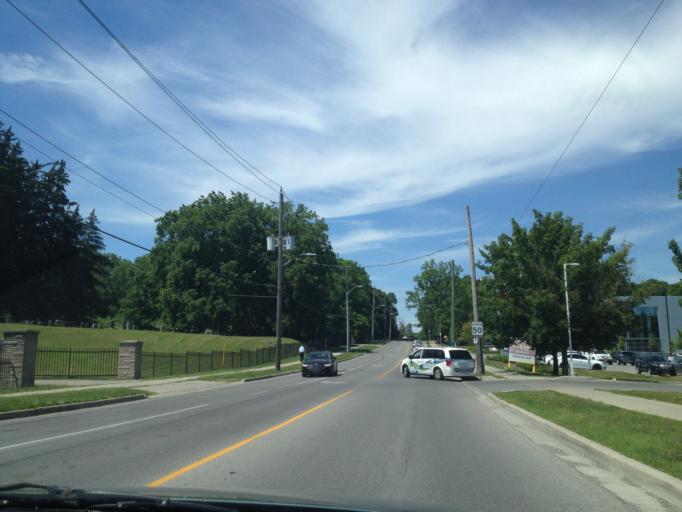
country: CA
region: Ontario
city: London
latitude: 42.9855
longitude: -81.2880
